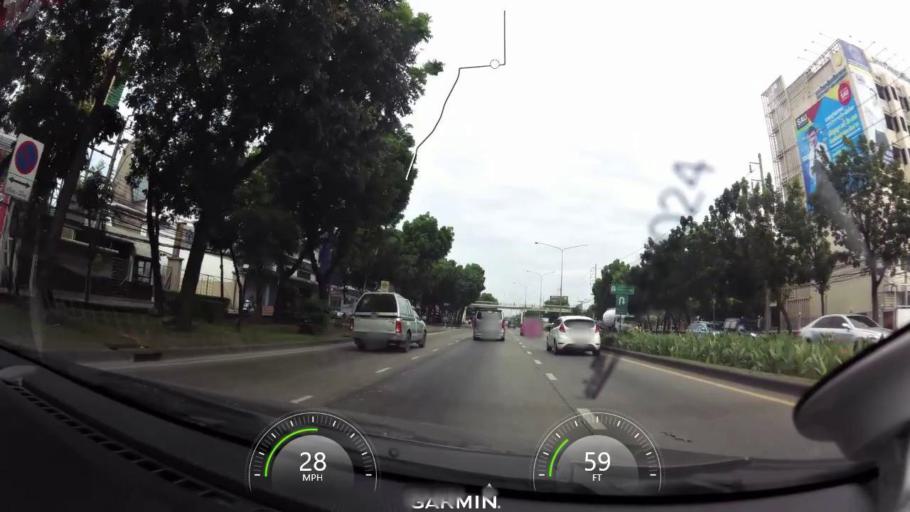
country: TH
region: Bangkok
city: Nong Khaem
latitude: 13.7066
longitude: 100.3575
